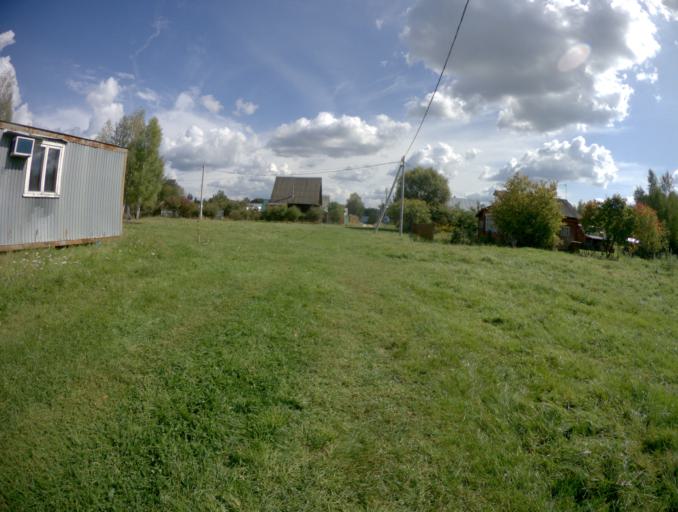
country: RU
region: Vladimir
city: Petushki
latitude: 55.8553
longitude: 39.3467
